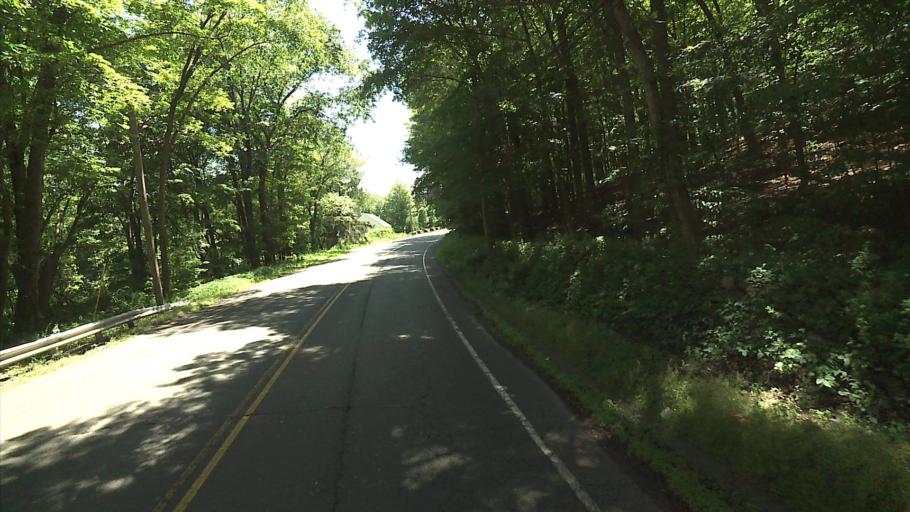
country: US
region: Connecticut
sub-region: New Haven County
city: Woodbridge
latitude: 41.3847
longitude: -72.9999
